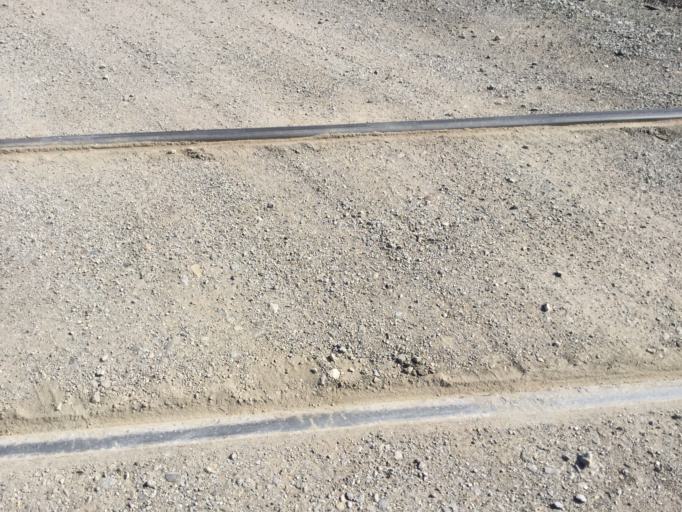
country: US
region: Kansas
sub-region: Cherokee County
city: Columbus
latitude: 37.1295
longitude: -94.7498
